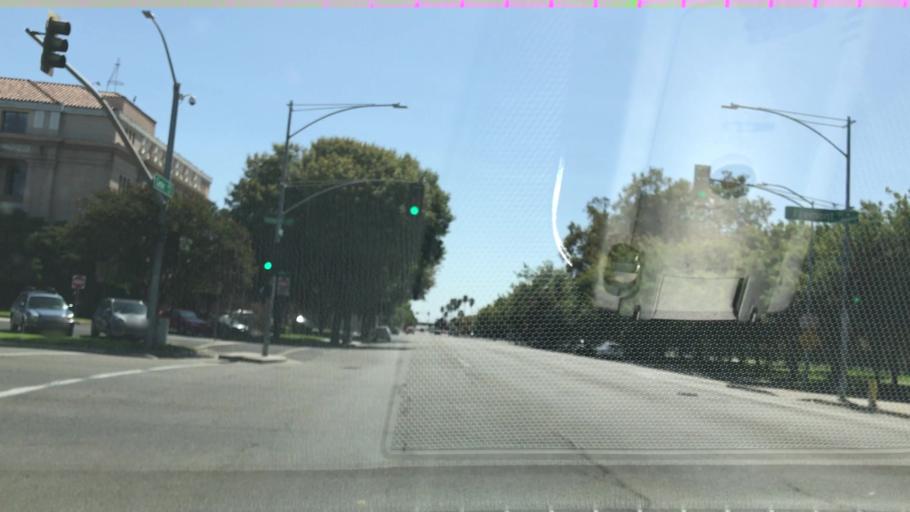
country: US
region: California
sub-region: San Joaquin County
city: Stockton
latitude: 37.9576
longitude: -121.2925
